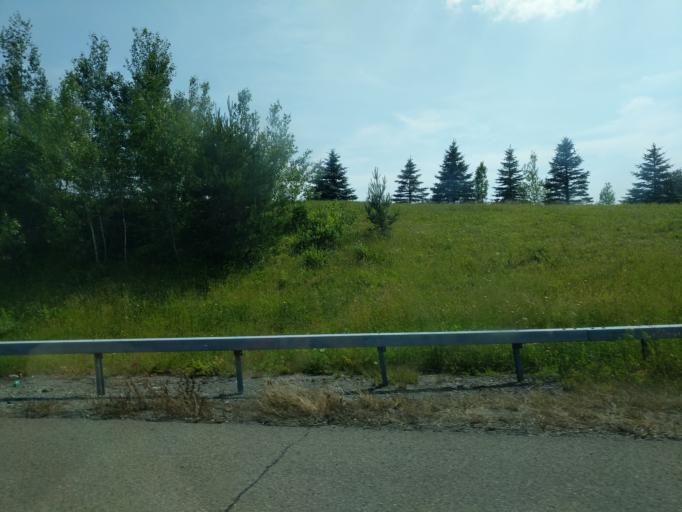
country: US
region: New York
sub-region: Sullivan County
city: Livingston Manor
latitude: 41.9076
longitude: -74.8224
